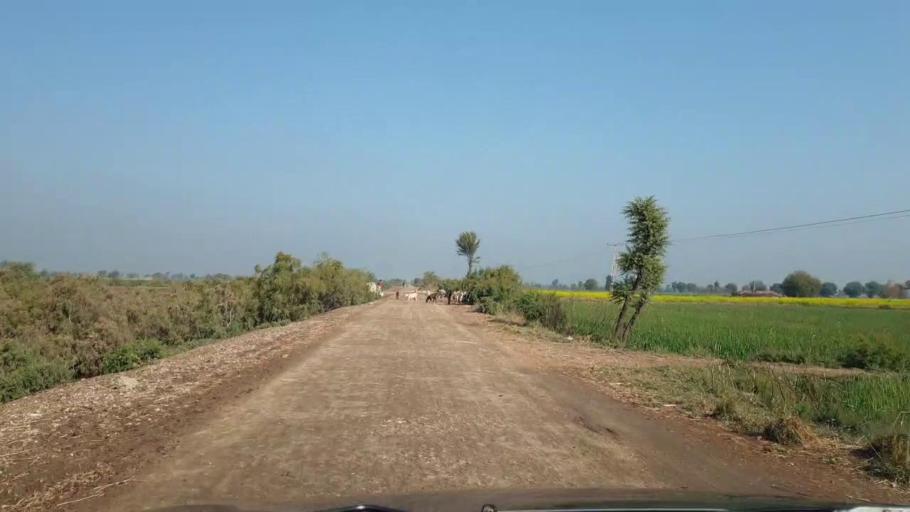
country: PK
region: Sindh
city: Sinjhoro
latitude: 26.0532
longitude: 68.7884
